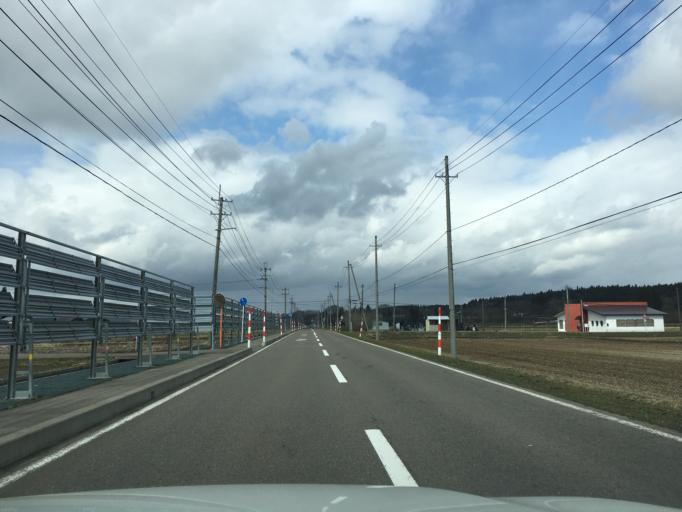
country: JP
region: Akita
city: Takanosu
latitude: 40.1366
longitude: 140.3537
